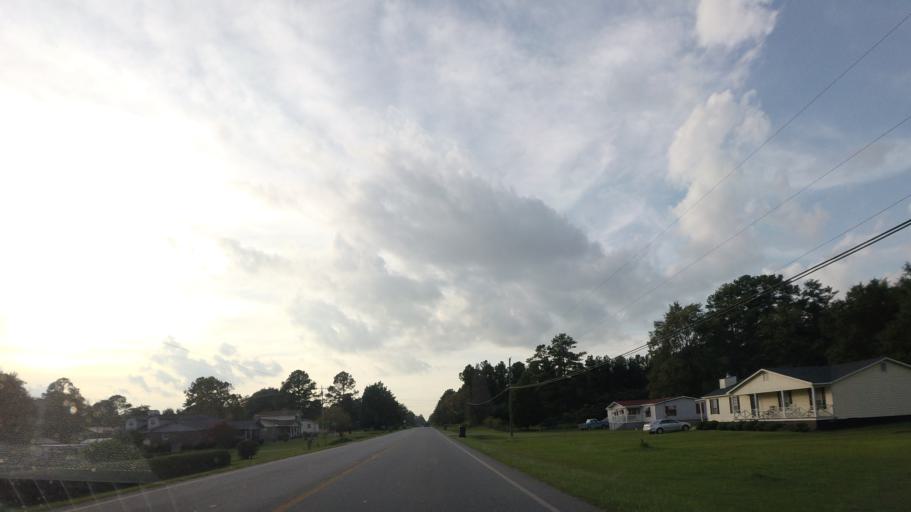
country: US
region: Georgia
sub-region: Wilkinson County
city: Gordon
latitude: 32.8915
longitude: -83.3556
